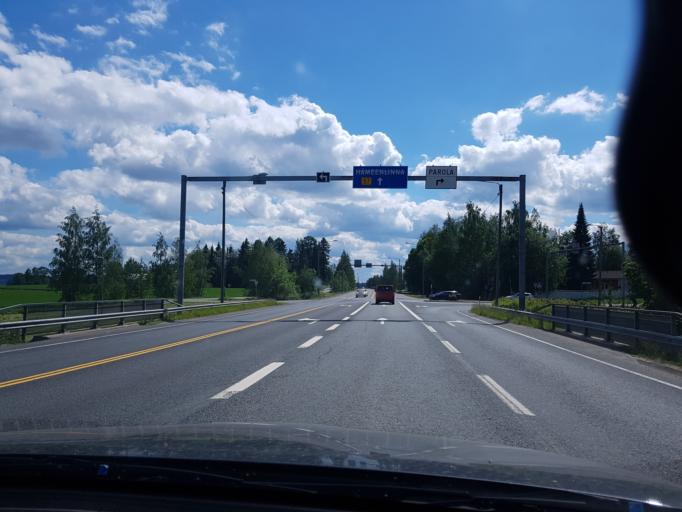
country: FI
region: Haeme
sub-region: Haemeenlinna
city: Parola
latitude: 61.0606
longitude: 24.3923
